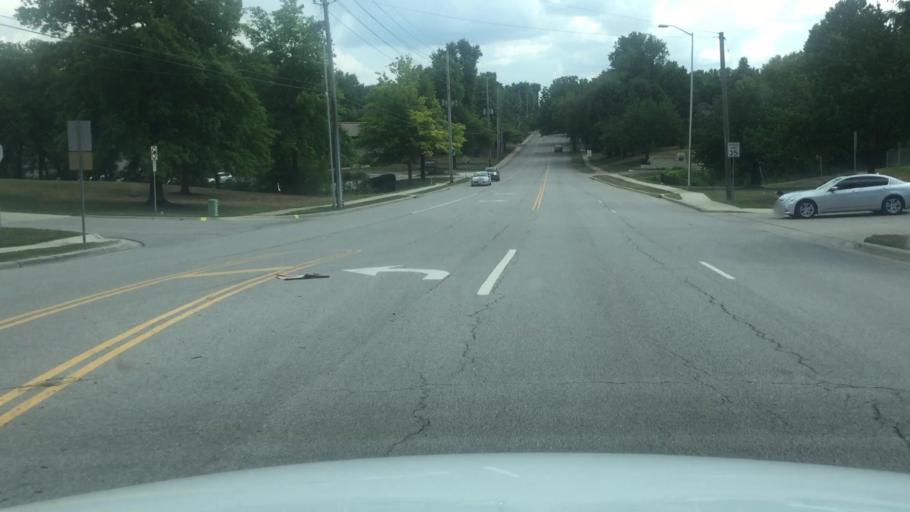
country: US
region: Kansas
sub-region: Johnson County
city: Lenexa
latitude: 38.9700
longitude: -94.7611
